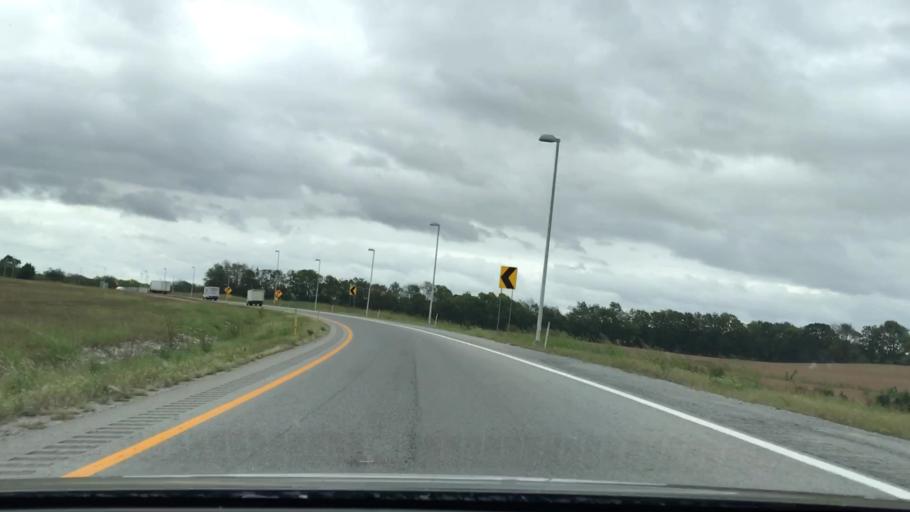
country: US
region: Kentucky
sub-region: Christian County
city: Fort Campbell North
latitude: 36.7384
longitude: -87.5073
